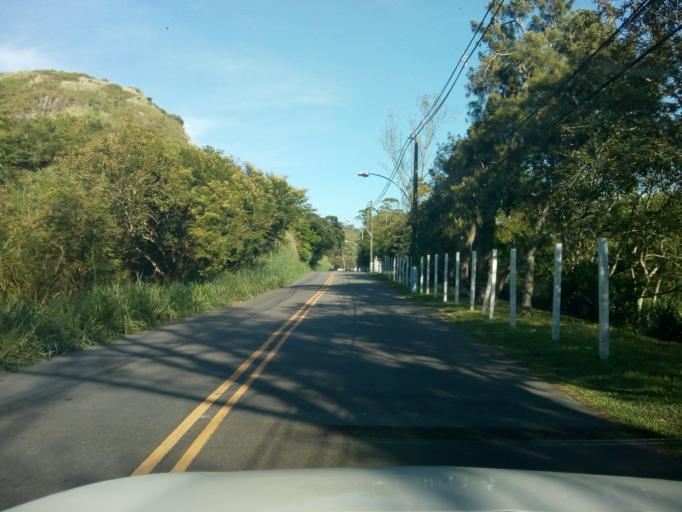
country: BR
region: Rio de Janeiro
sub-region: Nilopolis
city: Nilopolis
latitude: -23.0318
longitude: -43.4950
